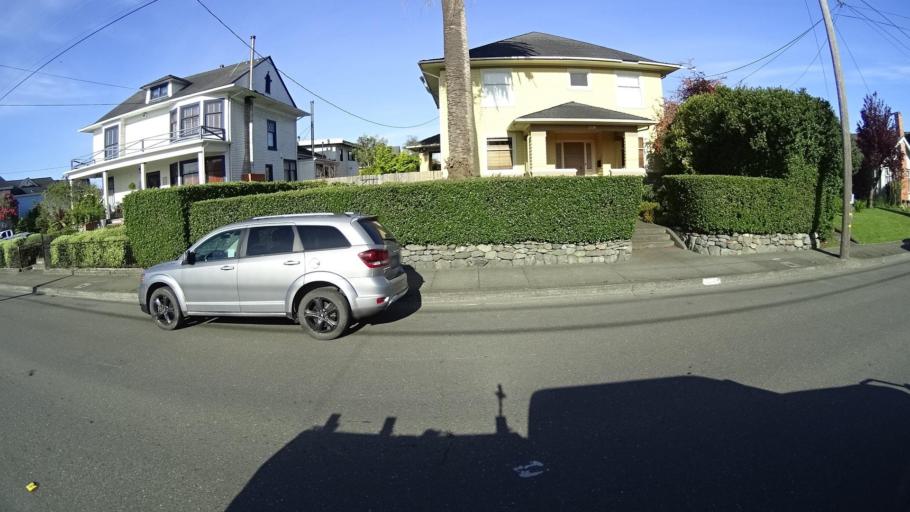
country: US
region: California
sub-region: Humboldt County
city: Eureka
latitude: 40.7872
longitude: -124.1646
